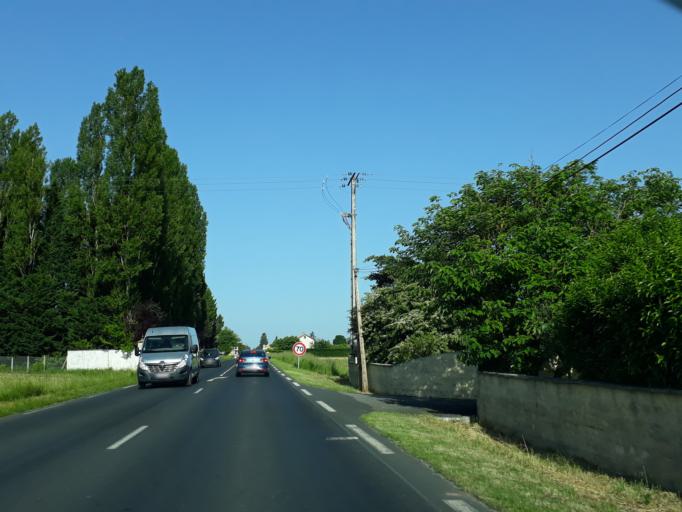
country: FR
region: Limousin
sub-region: Departement de la Correze
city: Larche
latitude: 45.1257
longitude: 1.3882
